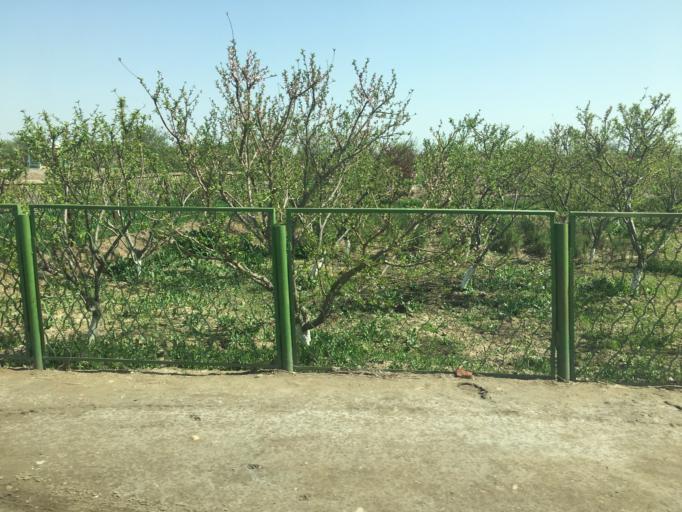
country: TM
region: Lebap
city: Turkmenabat
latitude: 38.9679
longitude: 63.6545
